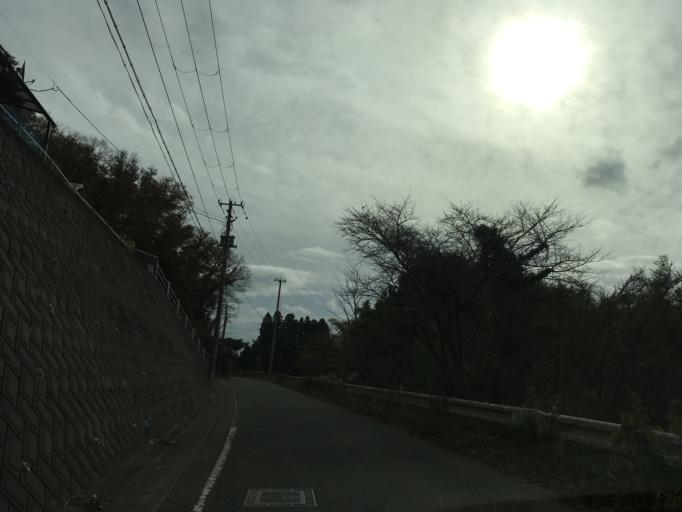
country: JP
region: Iwate
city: Ichinoseki
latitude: 38.7714
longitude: 141.2687
